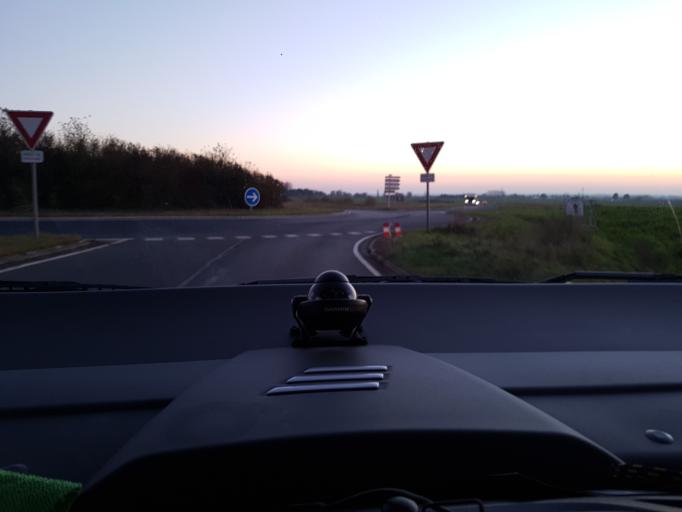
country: FR
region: Picardie
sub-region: Departement de la Somme
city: Nouvion
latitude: 50.2567
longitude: 1.7446
